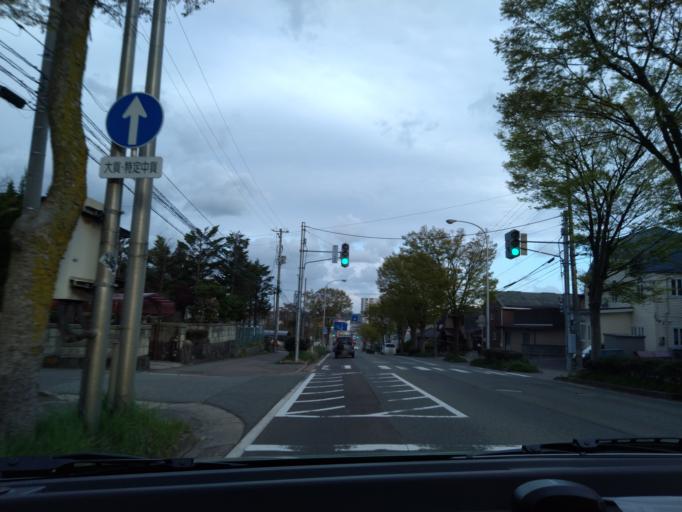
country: JP
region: Akita
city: Akita
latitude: 39.7320
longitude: 140.1433
